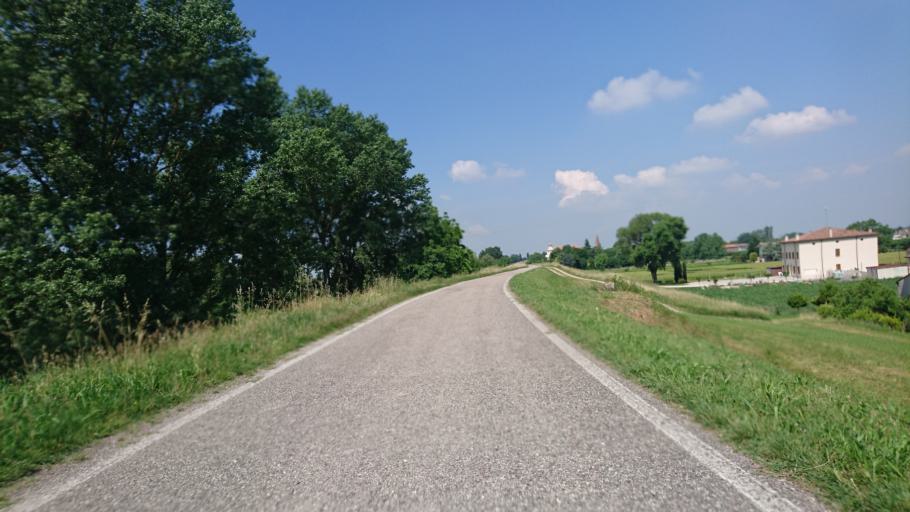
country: IT
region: Lombardy
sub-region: Provincia di Mantova
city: San Benedetto Po
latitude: 45.0796
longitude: 10.9681
